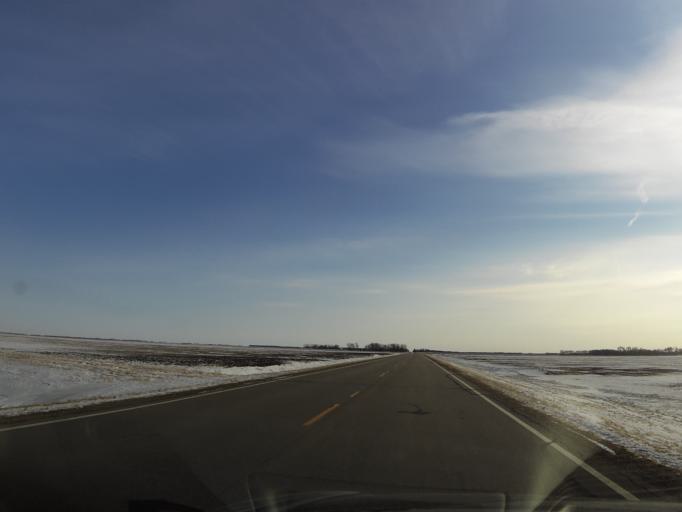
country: US
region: Minnesota
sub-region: Kittson County
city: Hallock
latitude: 48.5486
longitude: -97.1071
